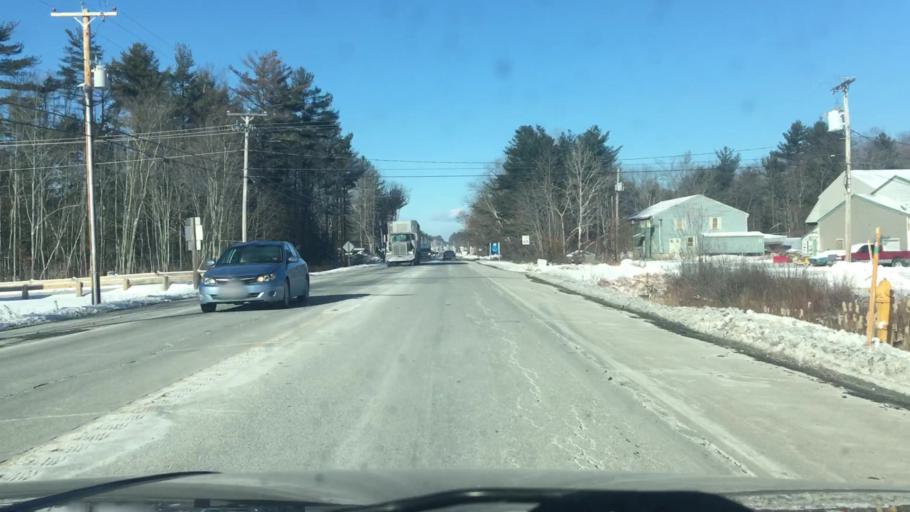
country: US
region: Maine
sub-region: York County
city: South Eliot
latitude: 43.1217
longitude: -70.7610
